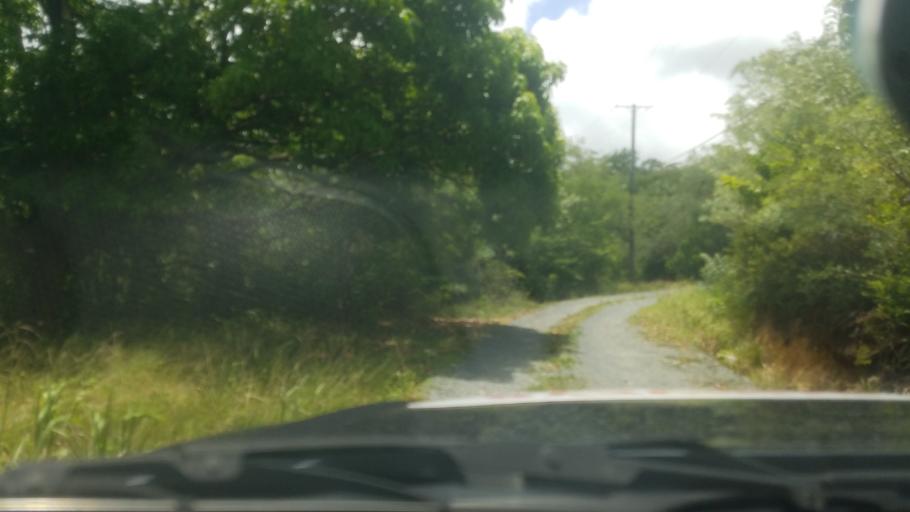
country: LC
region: Praslin
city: Praslin
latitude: 13.8662
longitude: -60.9053
